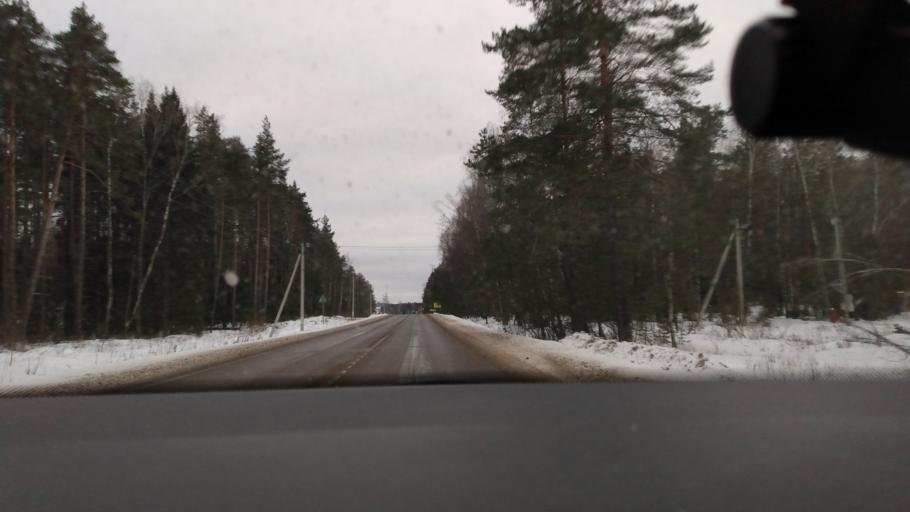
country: RU
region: Moskovskaya
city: Yegor'yevsk
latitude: 55.2785
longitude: 39.0831
